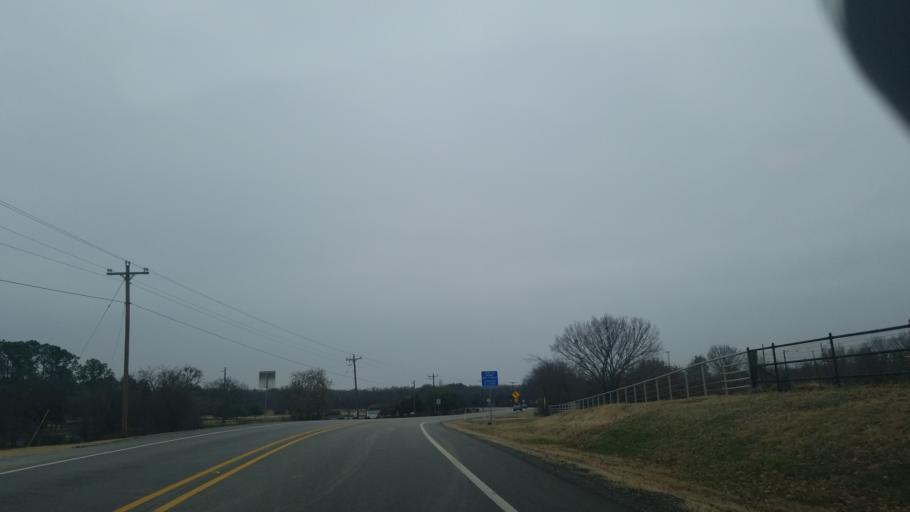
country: US
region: Texas
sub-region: Denton County
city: Argyle
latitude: 33.1363
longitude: -97.1485
